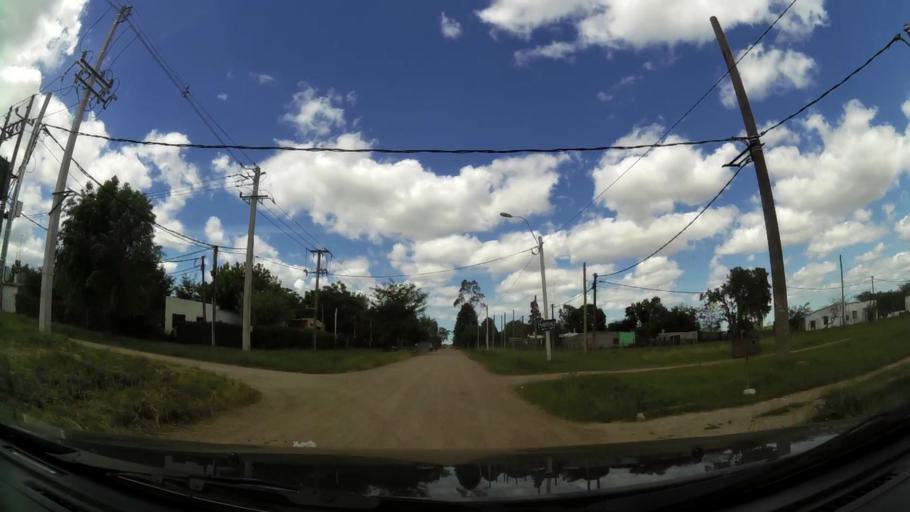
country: UY
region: Canelones
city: Colonia Nicolich
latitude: -34.8127
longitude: -56.0447
